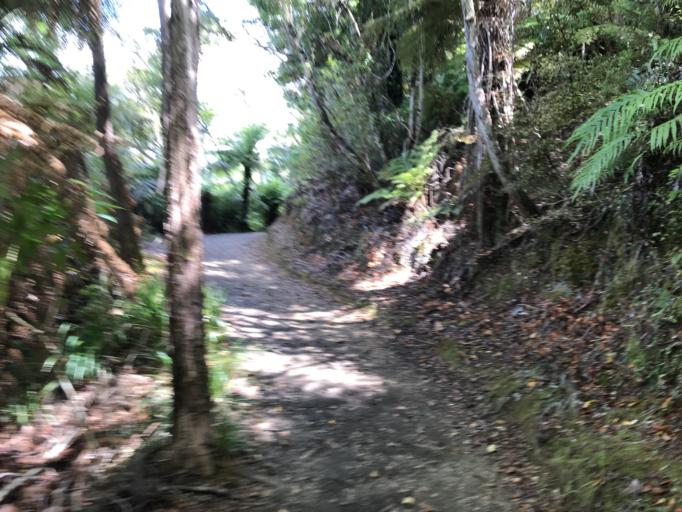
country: NZ
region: Marlborough
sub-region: Marlborough District
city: Picton
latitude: -41.2550
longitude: 173.9389
